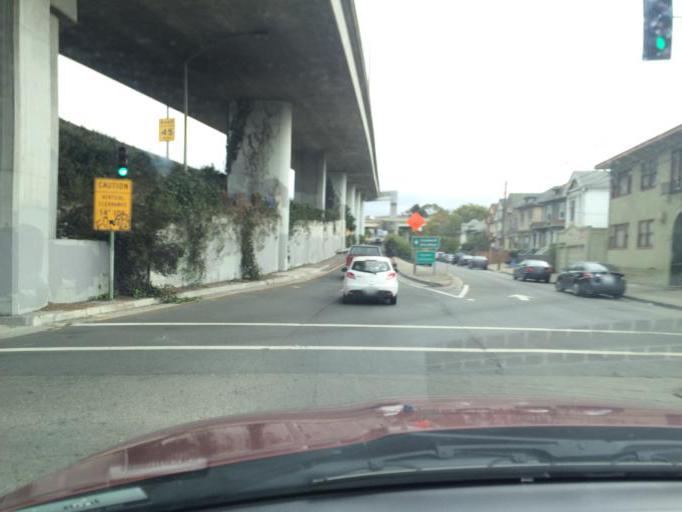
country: US
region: California
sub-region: Alameda County
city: Emeryville
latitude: 37.8249
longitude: -122.2725
